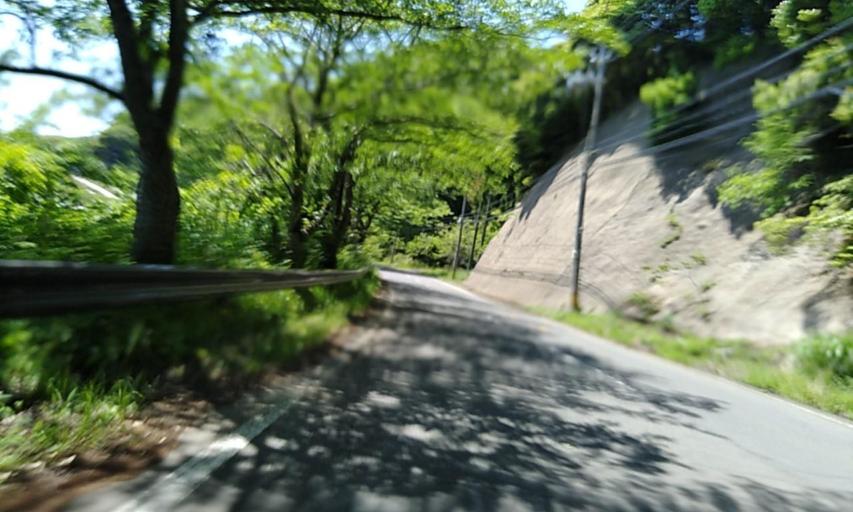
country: JP
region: Fukui
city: Obama
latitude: 35.5388
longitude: 135.7593
